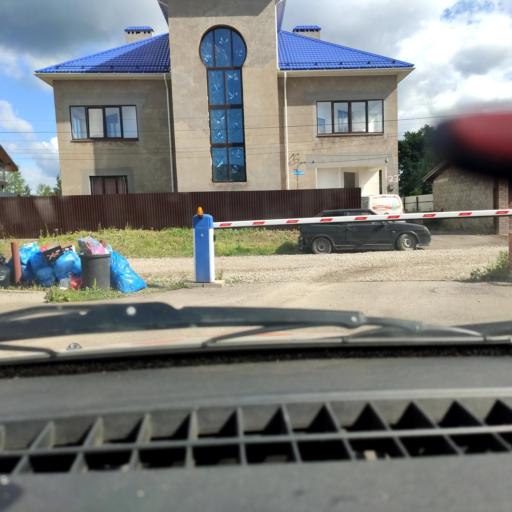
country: RU
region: Bashkortostan
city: Ufa
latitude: 54.7695
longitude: 55.9513
